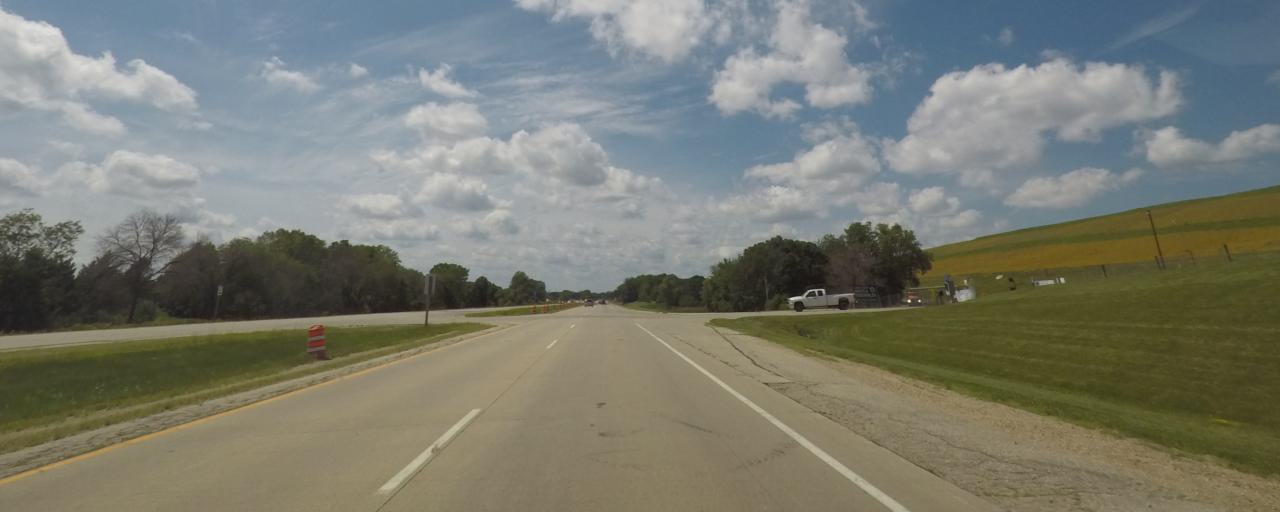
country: US
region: Wisconsin
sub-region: Dane County
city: McFarland
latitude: 43.0426
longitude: -89.2545
